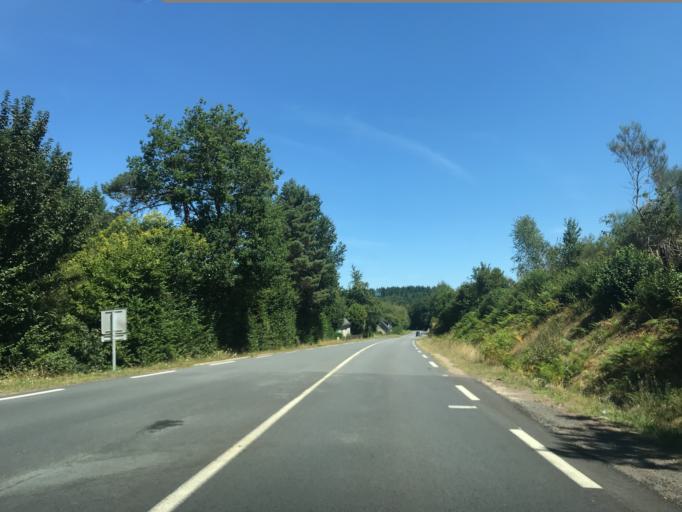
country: FR
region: Limousin
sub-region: Departement de la Correze
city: Egletons
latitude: 45.4430
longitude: 2.1027
